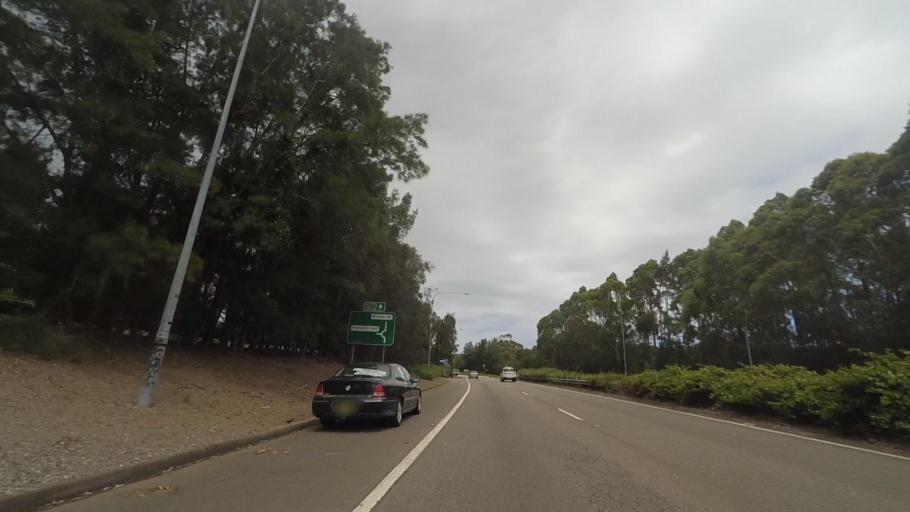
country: AU
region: New South Wales
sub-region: Wyong Shire
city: Berkeley Vale
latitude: -33.3503
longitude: 151.4324
